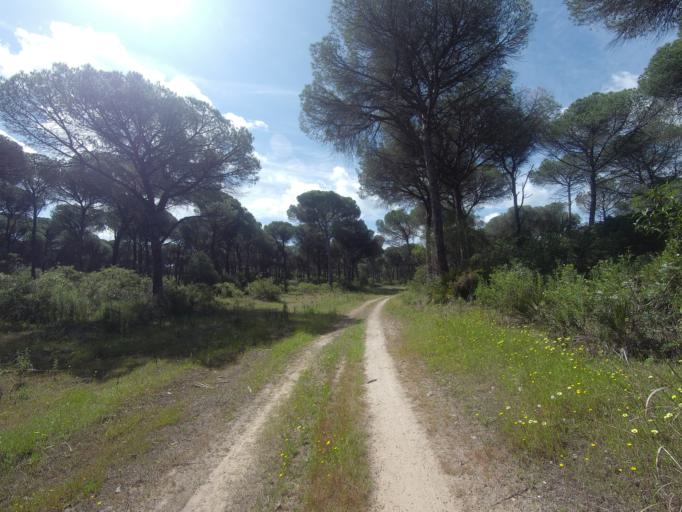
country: ES
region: Andalusia
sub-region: Provincia de Huelva
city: Aljaraque
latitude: 37.2286
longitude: -7.0669
